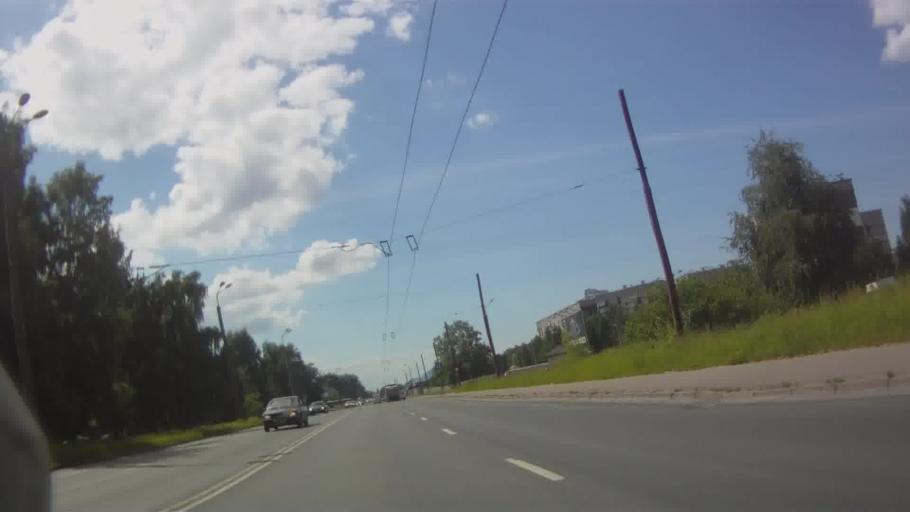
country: LV
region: Stopini
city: Ulbroka
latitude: 56.9472
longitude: 24.2004
